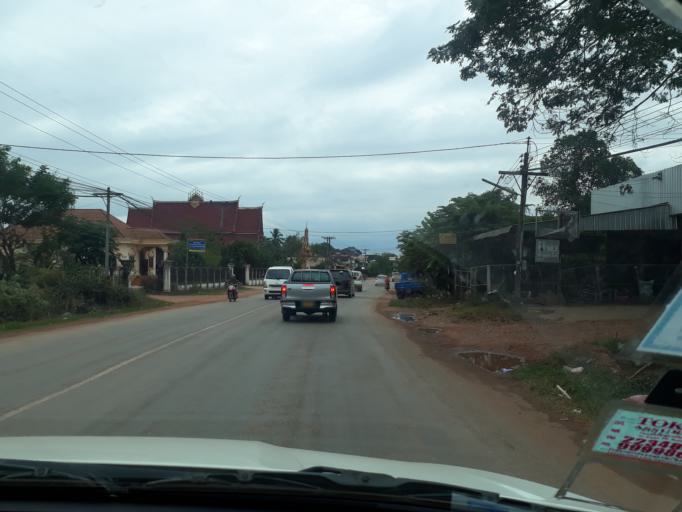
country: LA
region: Vientiane
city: Muang Phon-Hong
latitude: 18.3419
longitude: 102.4315
